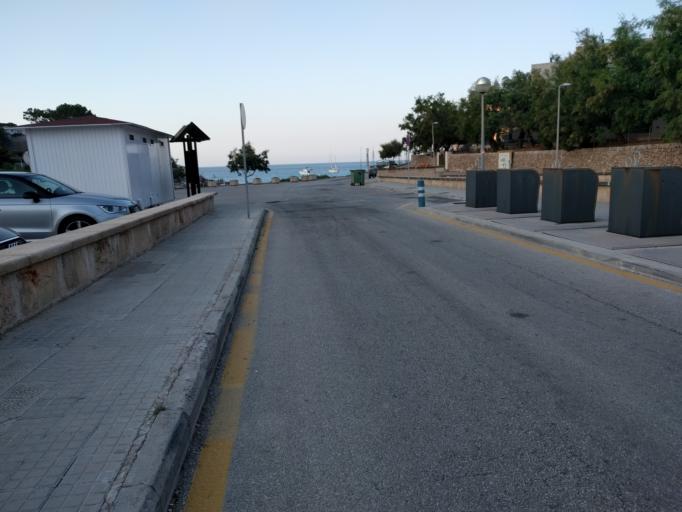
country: ES
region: Balearic Islands
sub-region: Illes Balears
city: Pollenca
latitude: 39.9192
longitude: 3.0569
